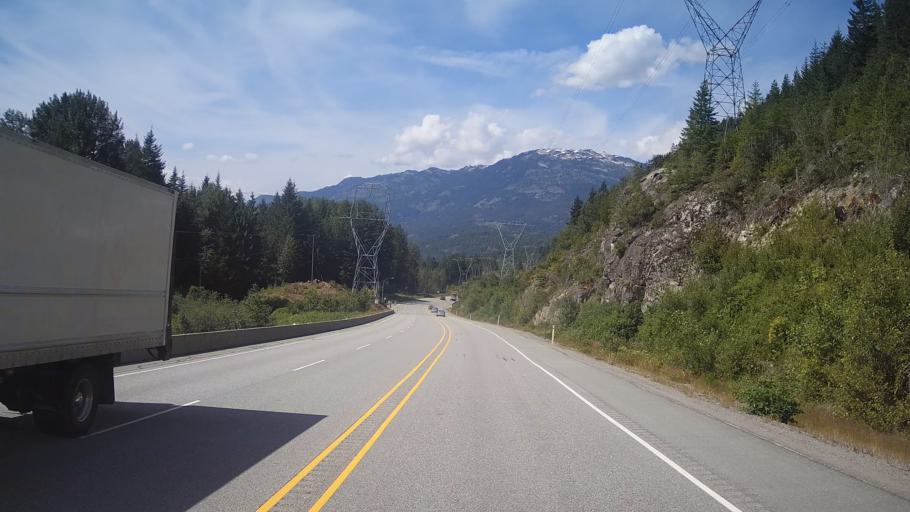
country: CA
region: British Columbia
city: Whistler
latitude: 50.0824
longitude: -123.0717
